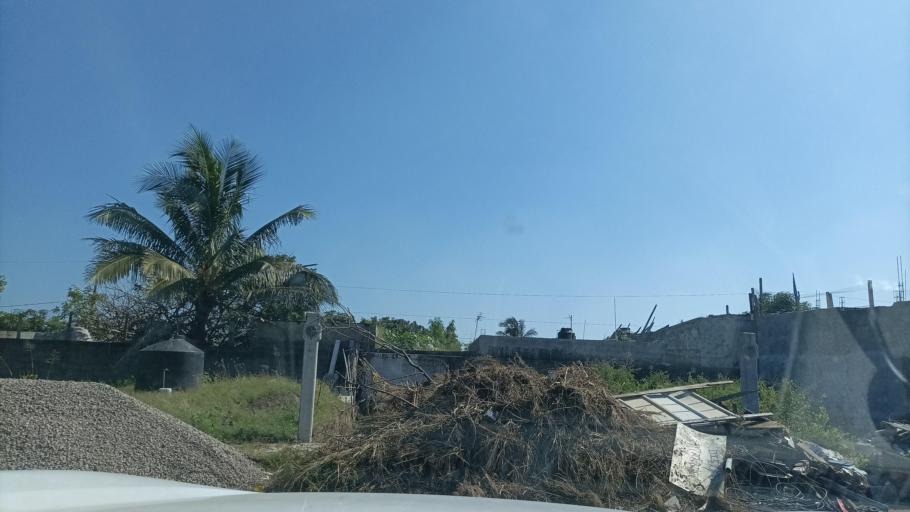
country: MX
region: Veracruz
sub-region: Veracruz
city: Rio Medio [Granja]
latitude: 19.2000
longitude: -96.1792
